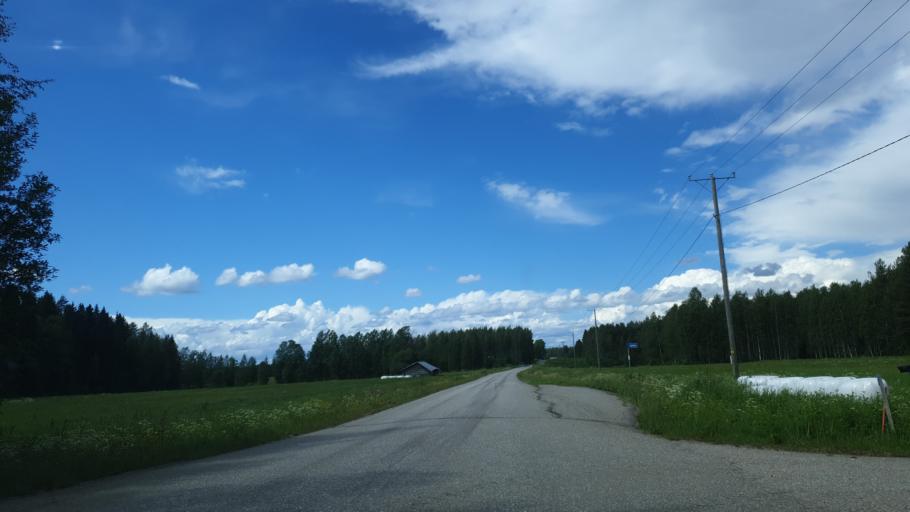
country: FI
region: Northern Savo
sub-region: Koillis-Savo
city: Kaavi
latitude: 62.9840
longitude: 28.7383
